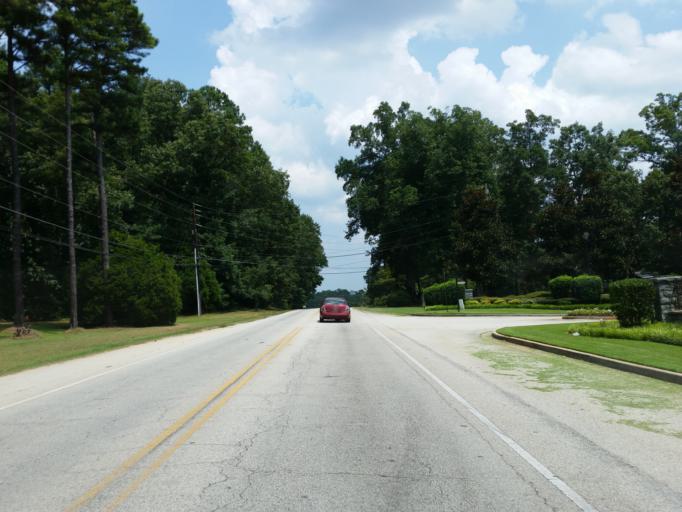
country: US
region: Georgia
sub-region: Henry County
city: Stockbridge
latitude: 33.4995
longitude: -84.2524
